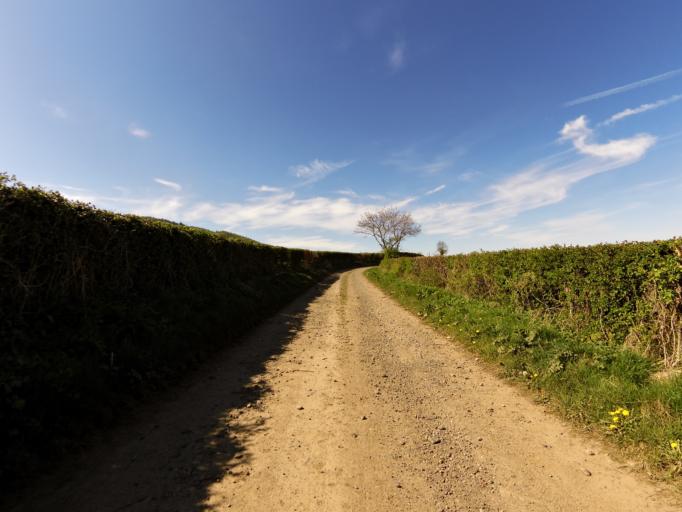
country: GB
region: Scotland
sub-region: Fife
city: Cupar
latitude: 56.4057
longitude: -3.0458
